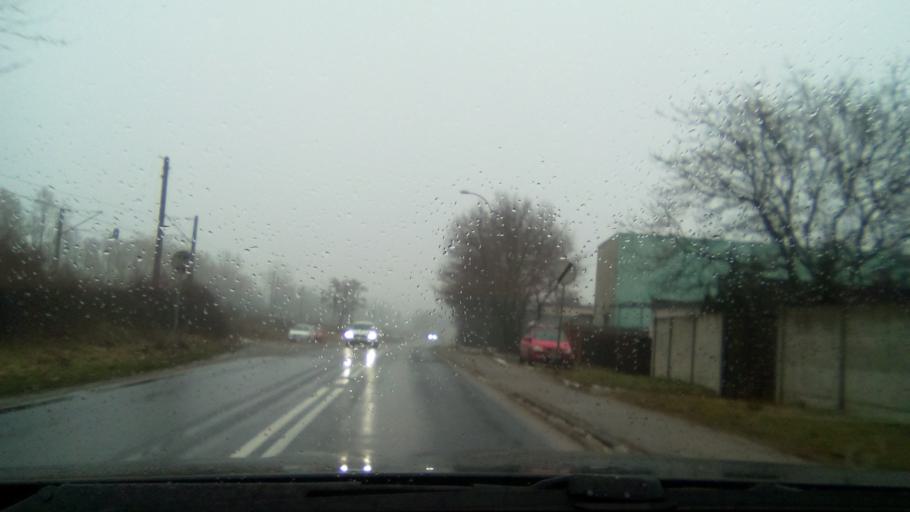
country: PL
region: Greater Poland Voivodeship
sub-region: Powiat poznanski
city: Swarzedz
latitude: 52.3995
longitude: 17.0481
